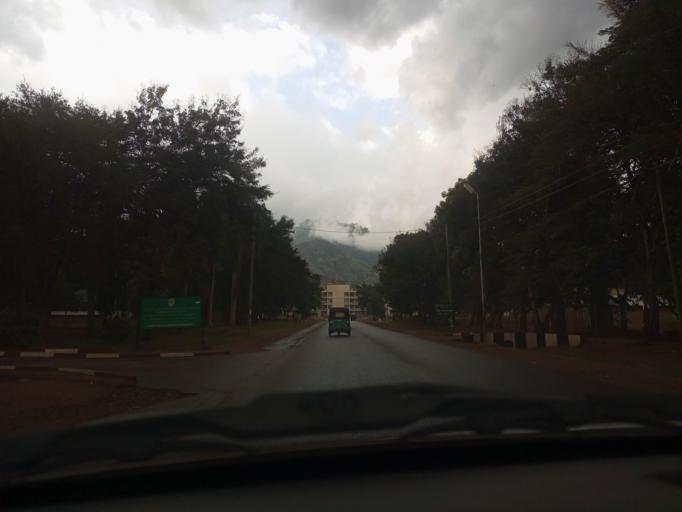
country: TZ
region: Morogoro
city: Morogoro
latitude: -6.8496
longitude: 37.6577
